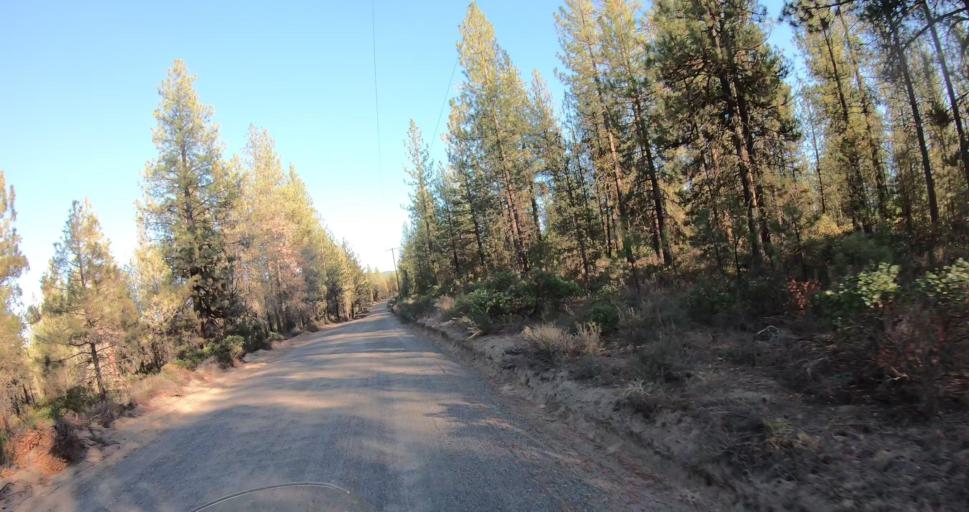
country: US
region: Oregon
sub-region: Deschutes County
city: La Pine
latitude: 43.7205
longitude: -121.3974
